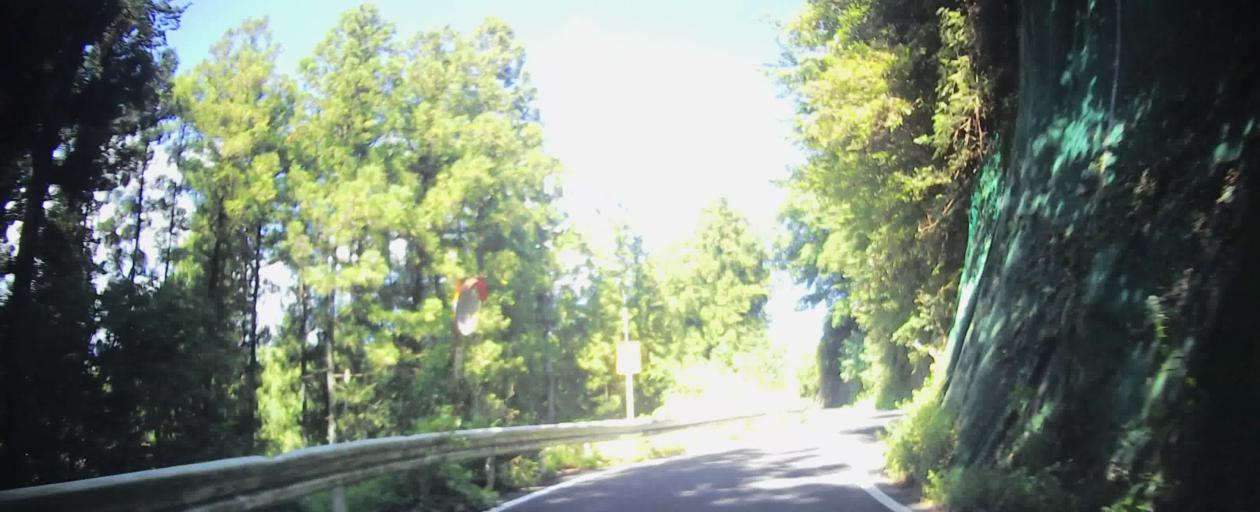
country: JP
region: Gunma
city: Kanekomachi
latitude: 36.4056
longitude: 138.9493
